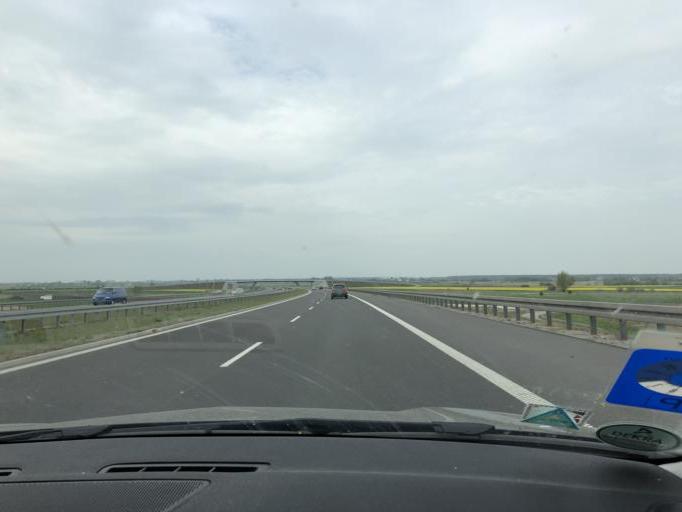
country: PL
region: Subcarpathian Voivodeship
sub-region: Powiat przeworski
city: Rozborz
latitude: 50.0688
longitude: 22.5581
